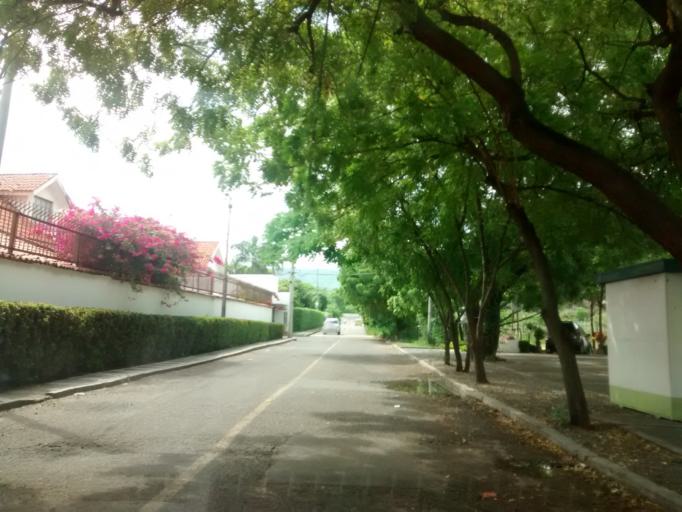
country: CO
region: Cundinamarca
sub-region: Girardot
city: Girardot City
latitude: 4.3164
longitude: -74.8051
